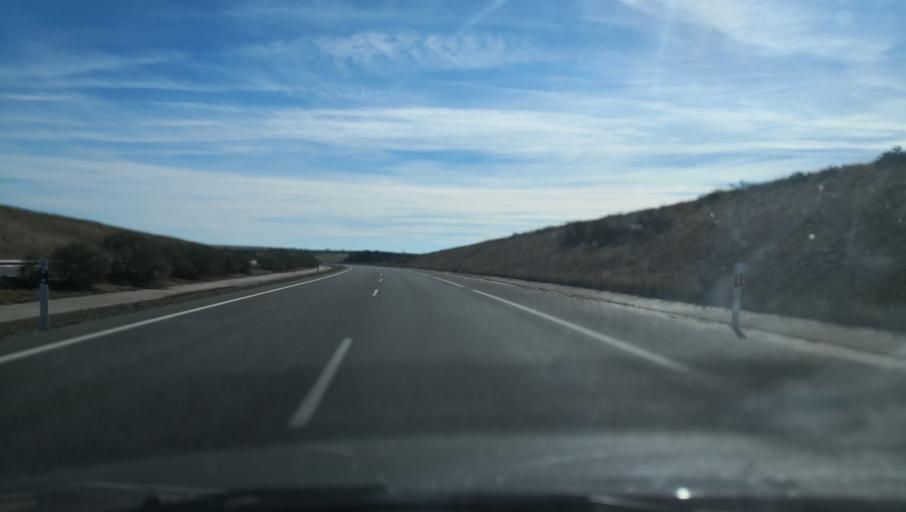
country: ES
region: Castille and Leon
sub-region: Provincia de Avila
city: Gimialcon
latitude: 40.8763
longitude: -5.1340
